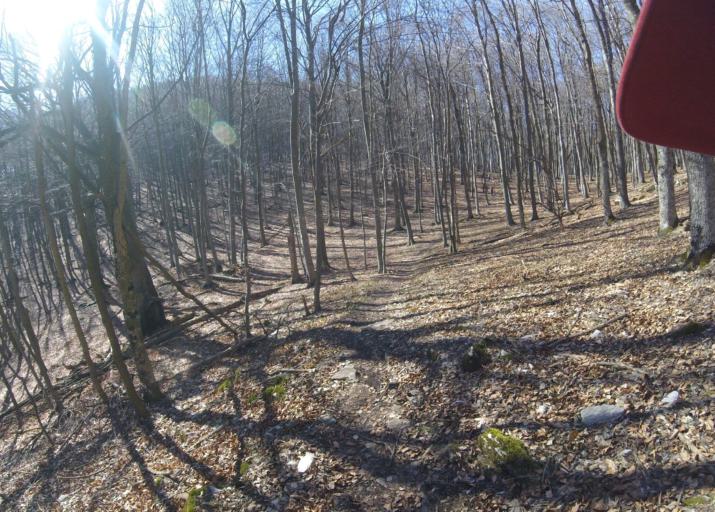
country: HU
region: Heves
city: Szilvasvarad
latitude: 48.0512
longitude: 20.4302
